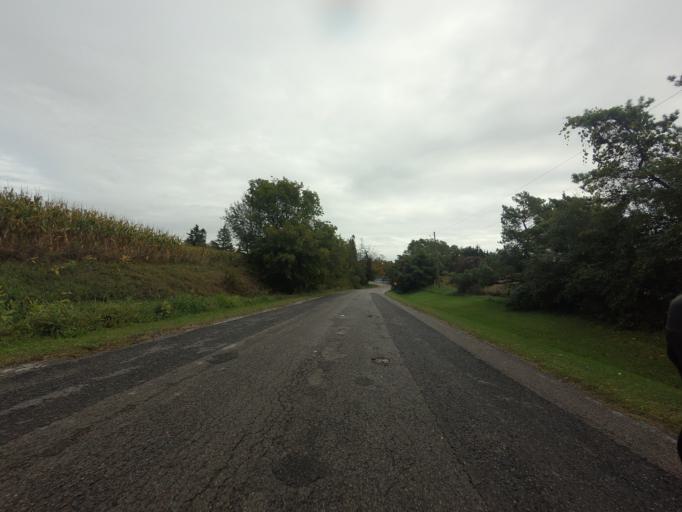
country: CA
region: Ontario
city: Cobourg
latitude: 43.9047
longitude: -78.4627
